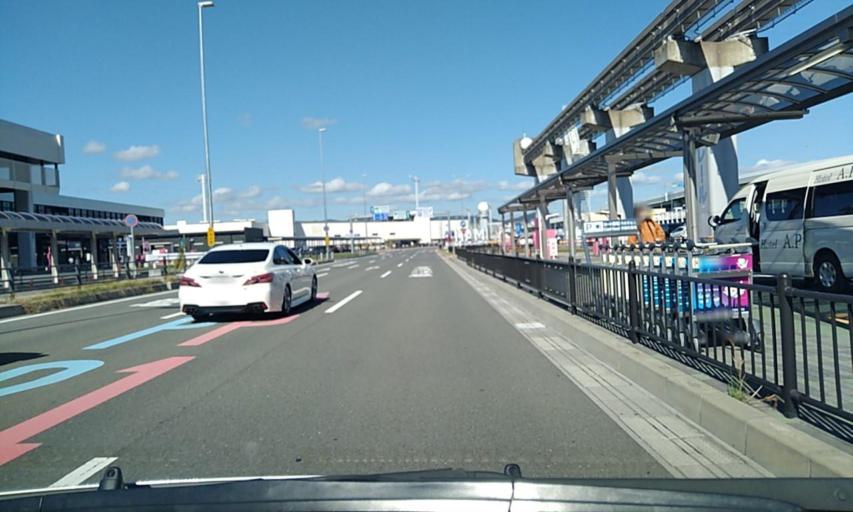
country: JP
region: Osaka
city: Toyonaka
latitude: 34.7921
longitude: 135.4409
